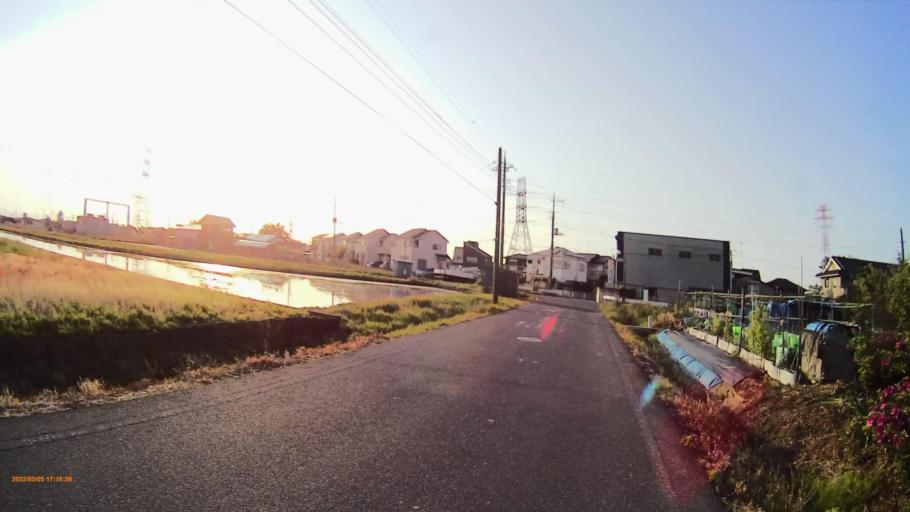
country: JP
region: Saitama
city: Kurihashi
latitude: 36.1318
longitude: 139.7072
